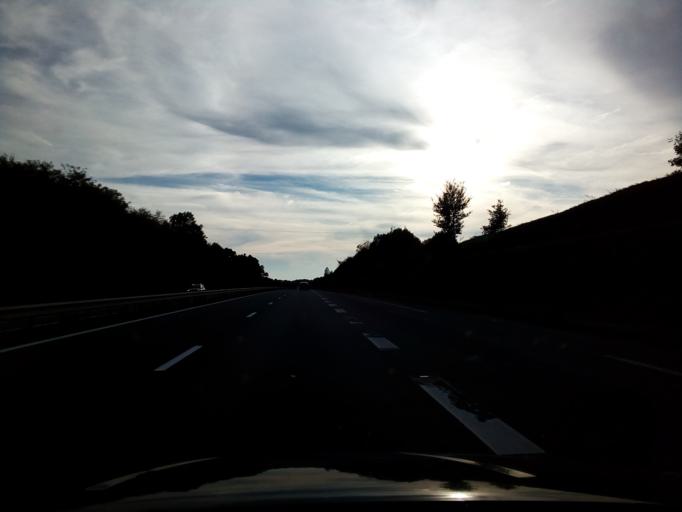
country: FR
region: Poitou-Charentes
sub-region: Departement de la Charente
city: Chasseneuil-sur-Bonnieure
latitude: 45.8099
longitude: 0.4475
